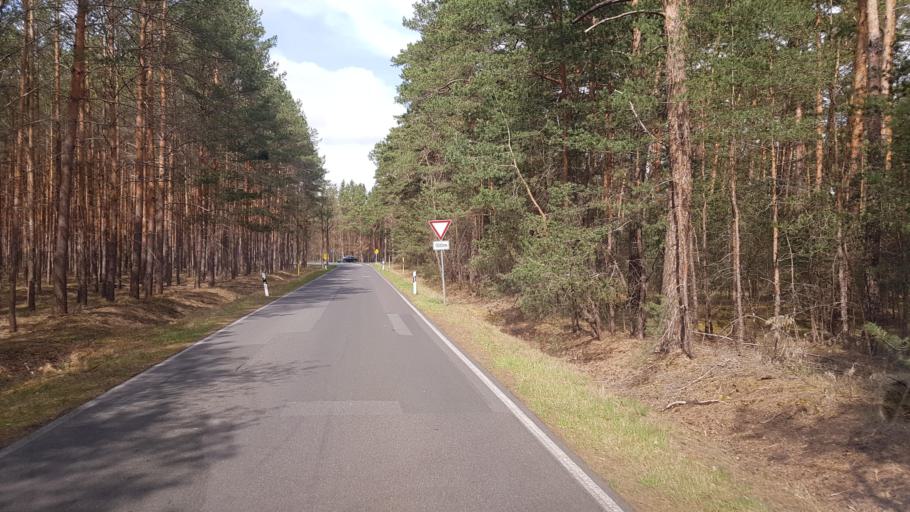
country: DE
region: Brandenburg
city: Luckenwalde
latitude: 52.1417
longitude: 13.1847
